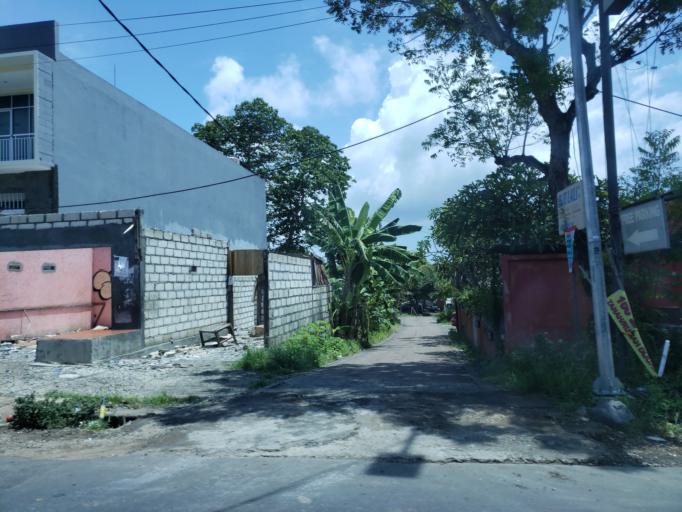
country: ID
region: Bali
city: Jimbaran
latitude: -8.7910
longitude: 115.1639
